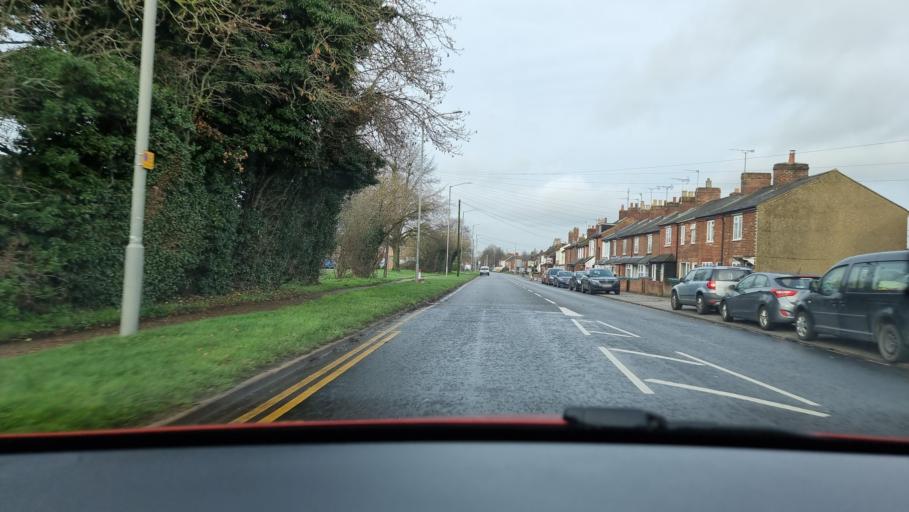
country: GB
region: England
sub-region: Buckinghamshire
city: Aylesbury
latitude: 51.8233
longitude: -0.8149
